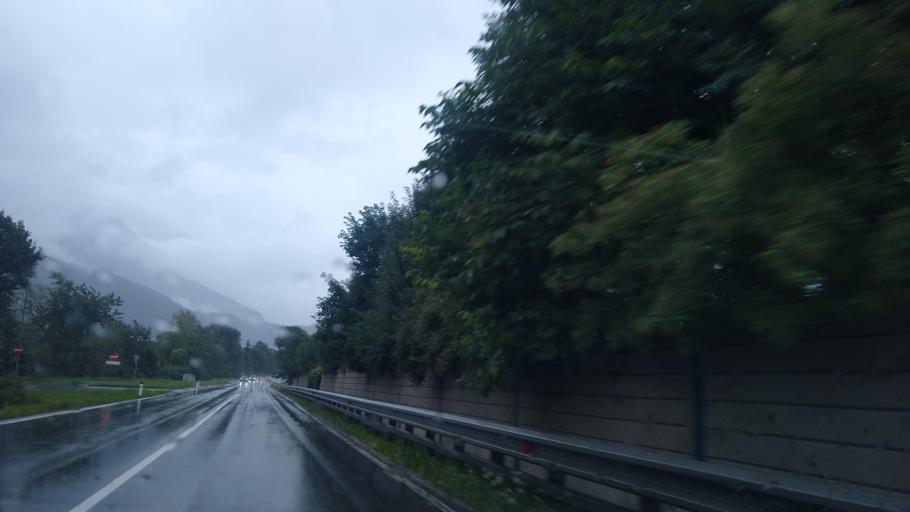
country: AT
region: Tyrol
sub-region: Politischer Bezirk Schwaz
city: Buch bei Jenbach
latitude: 47.3763
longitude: 11.7507
